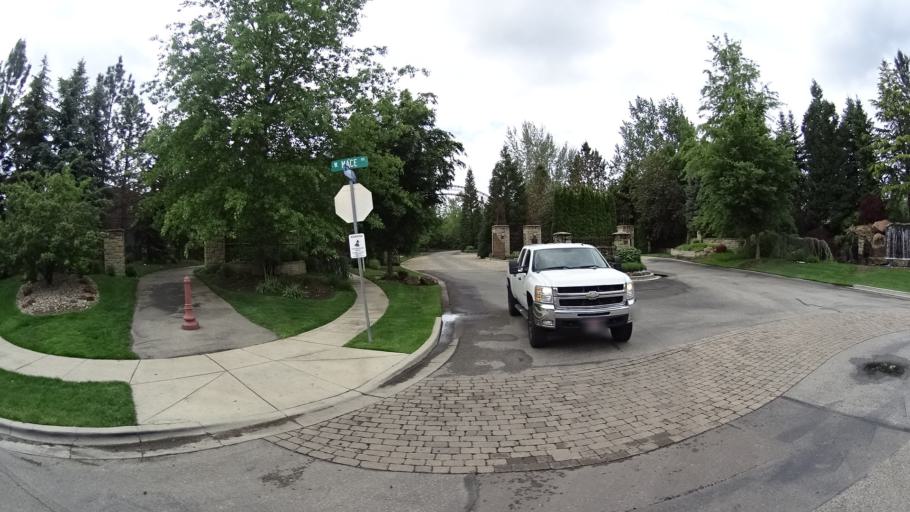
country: US
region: Idaho
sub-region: Ada County
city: Eagle
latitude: 43.6856
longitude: -116.3670
